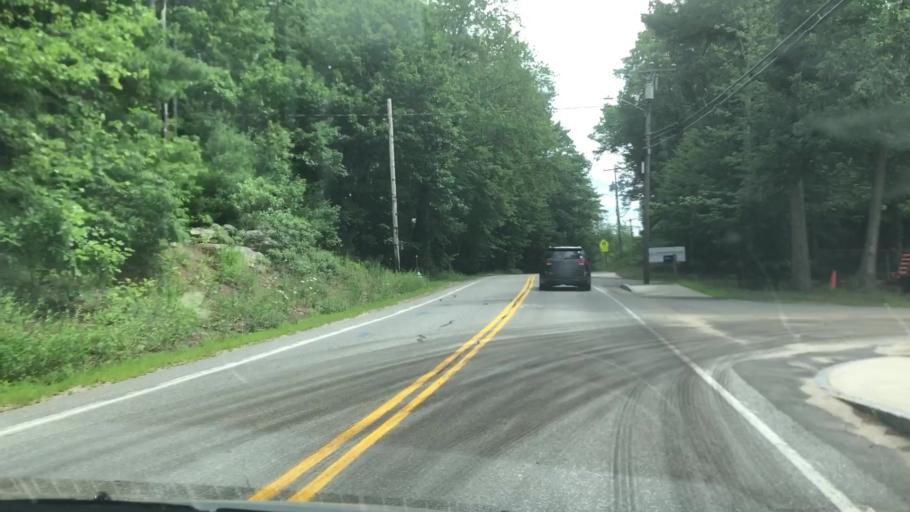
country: US
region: New Hampshire
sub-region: Hillsborough County
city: Bedford
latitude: 42.9398
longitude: -71.5173
